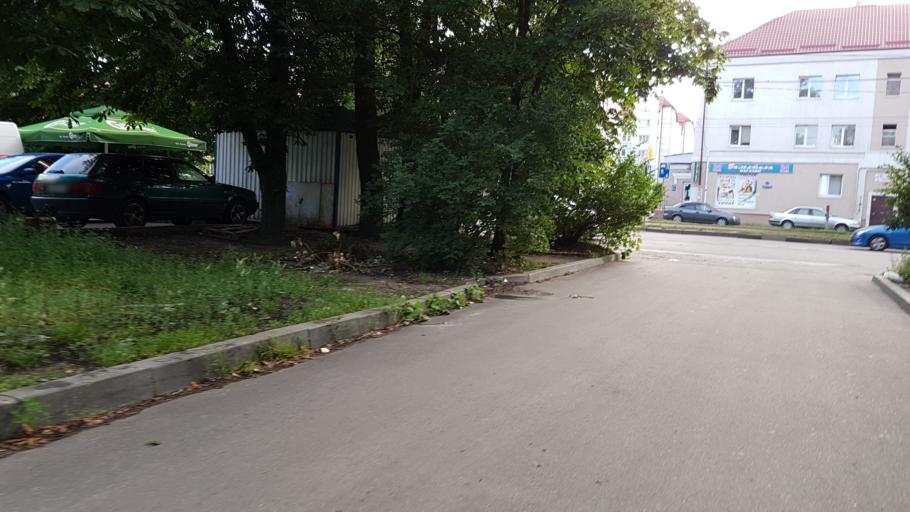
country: RU
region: Kaliningrad
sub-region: Gorod Kaliningrad
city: Kaliningrad
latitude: 54.6912
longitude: 20.5241
